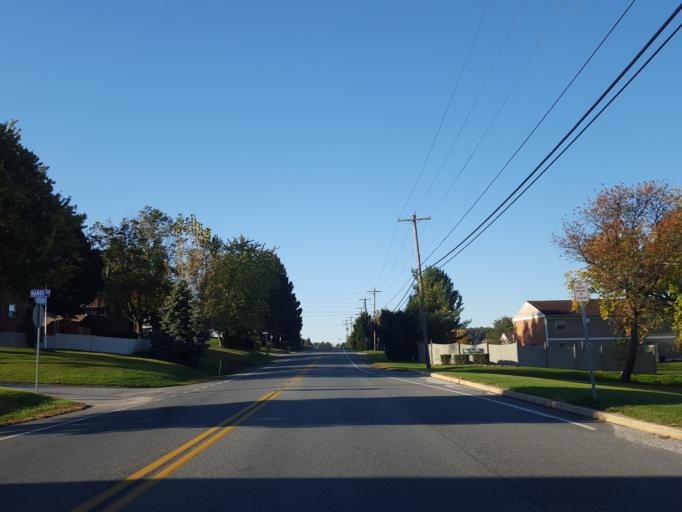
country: US
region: Pennsylvania
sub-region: York County
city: Yoe
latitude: 39.9140
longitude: -76.6320
